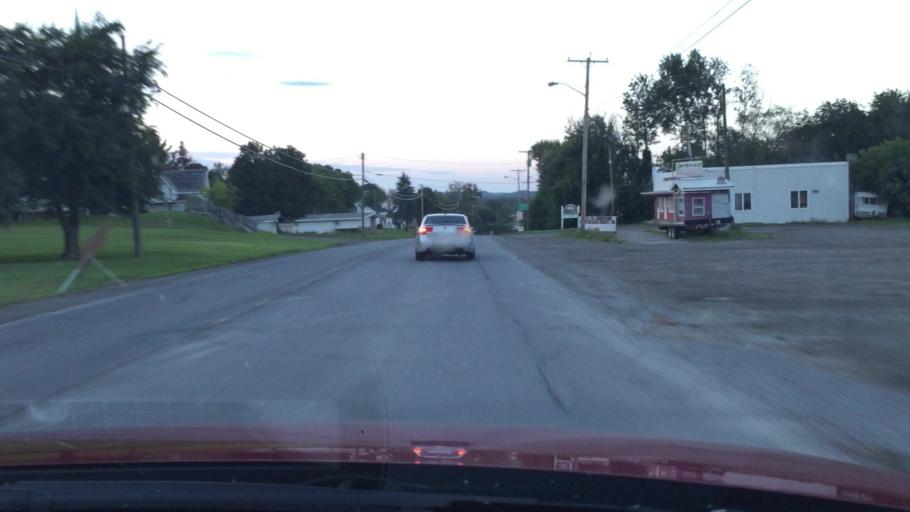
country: US
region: Maine
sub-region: Aroostook County
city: Easton
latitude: 46.5084
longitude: -67.8685
